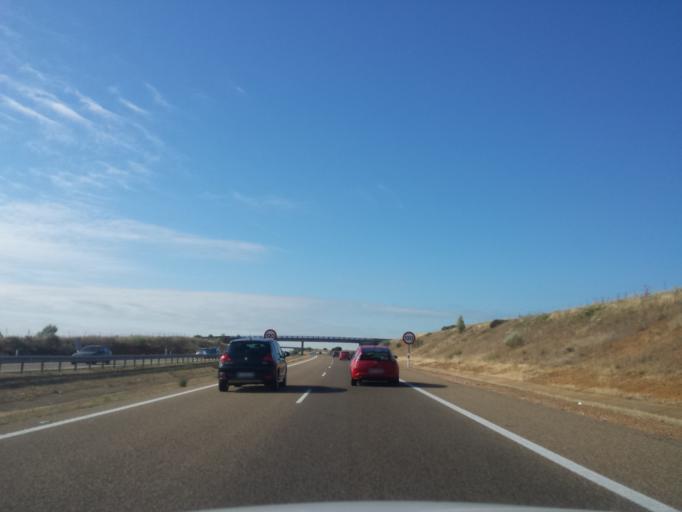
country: ES
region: Castille and Leon
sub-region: Provincia de Leon
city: Valdevimbre
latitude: 42.3932
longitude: -5.5961
